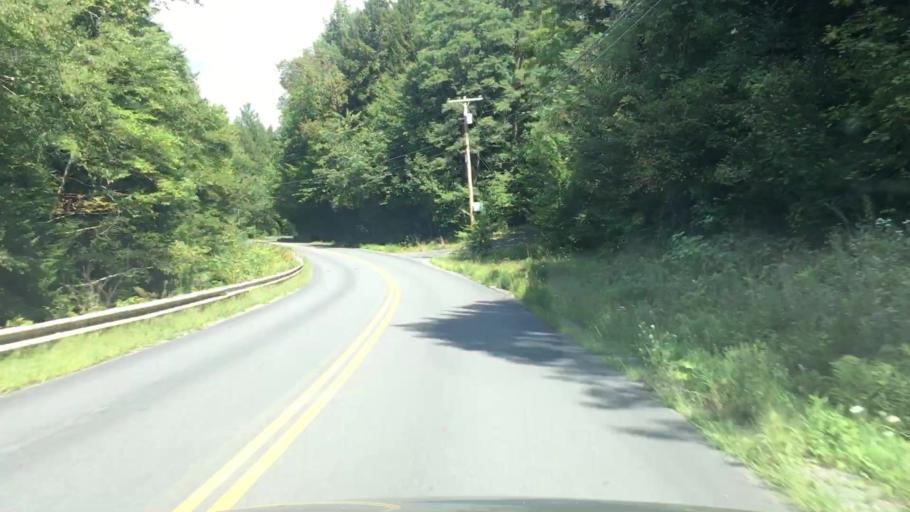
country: US
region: Vermont
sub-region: Windham County
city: West Brattleboro
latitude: 42.8014
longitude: -72.6189
